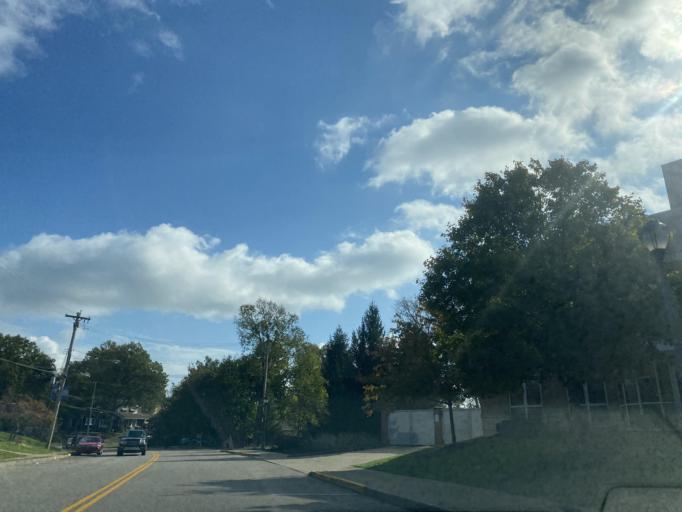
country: US
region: Kentucky
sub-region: Campbell County
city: Fort Thomas
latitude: 39.0855
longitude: -84.4505
